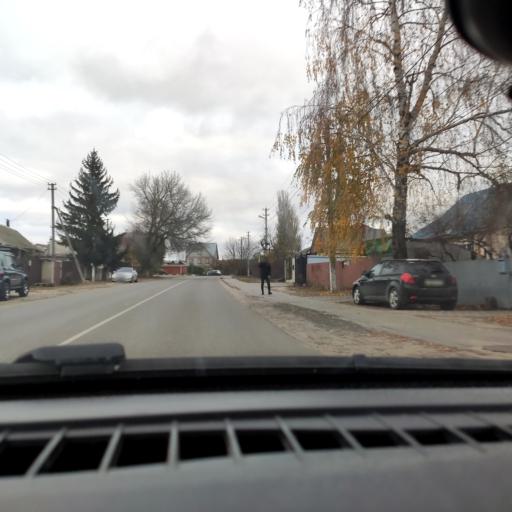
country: RU
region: Voronezj
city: Podgornoye
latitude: 51.7383
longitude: 39.1607
